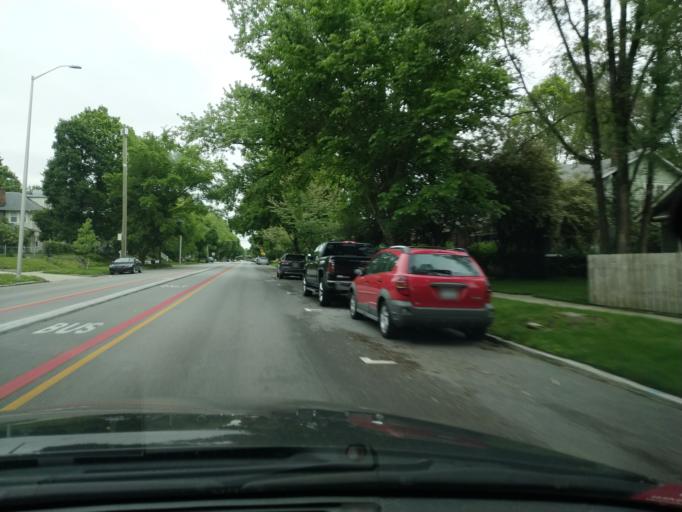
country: US
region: Indiana
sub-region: Marion County
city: Broad Ripple
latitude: 39.8345
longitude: -86.1451
